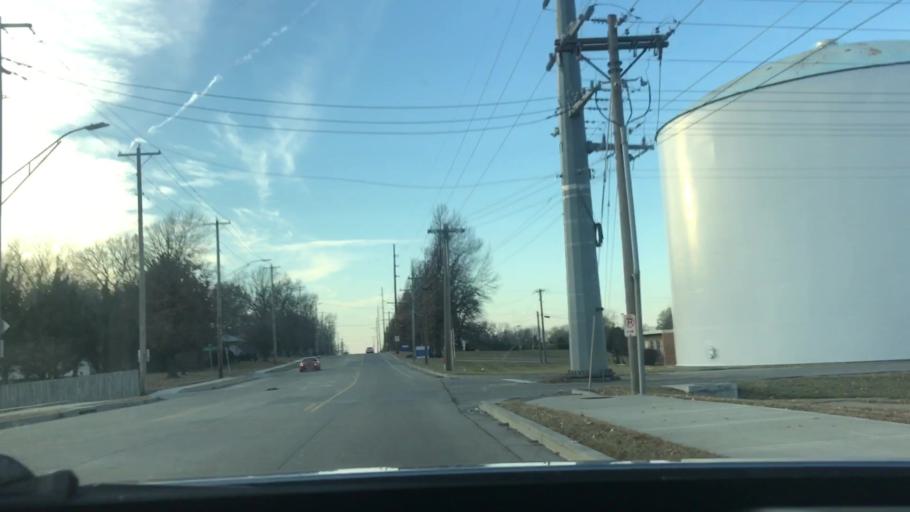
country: US
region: Missouri
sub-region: Jackson County
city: Independence
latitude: 39.0575
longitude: -94.4184
